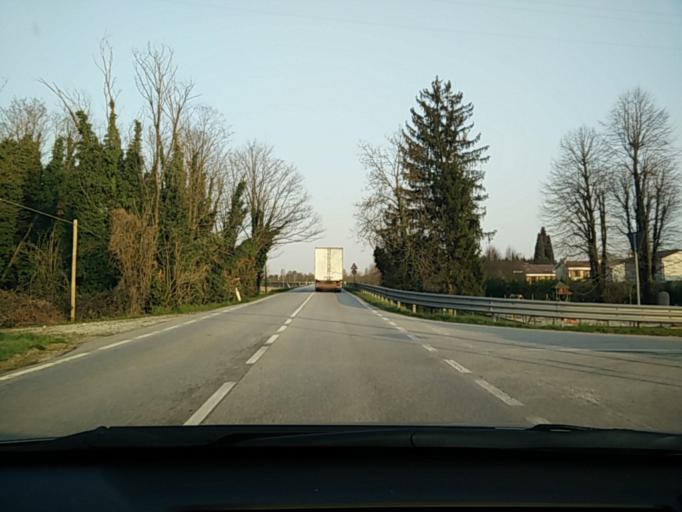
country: IT
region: Veneto
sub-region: Provincia di Treviso
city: Saletto-San Bartolomeo
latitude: 45.7095
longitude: 12.4269
